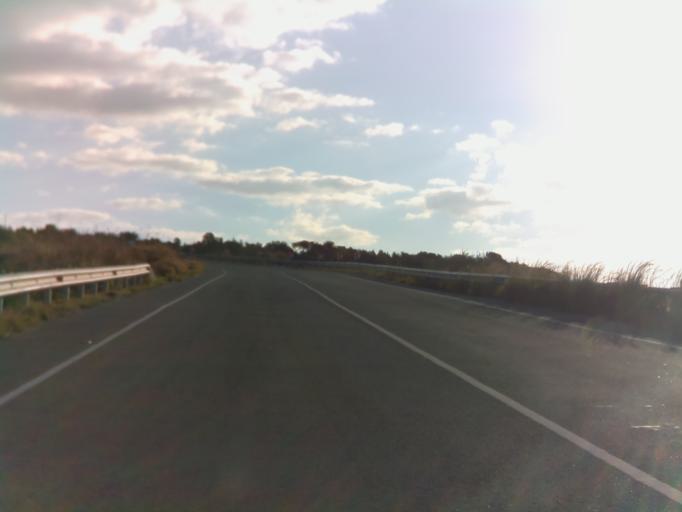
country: CY
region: Pafos
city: Pegeia
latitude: 34.8875
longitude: 32.3533
